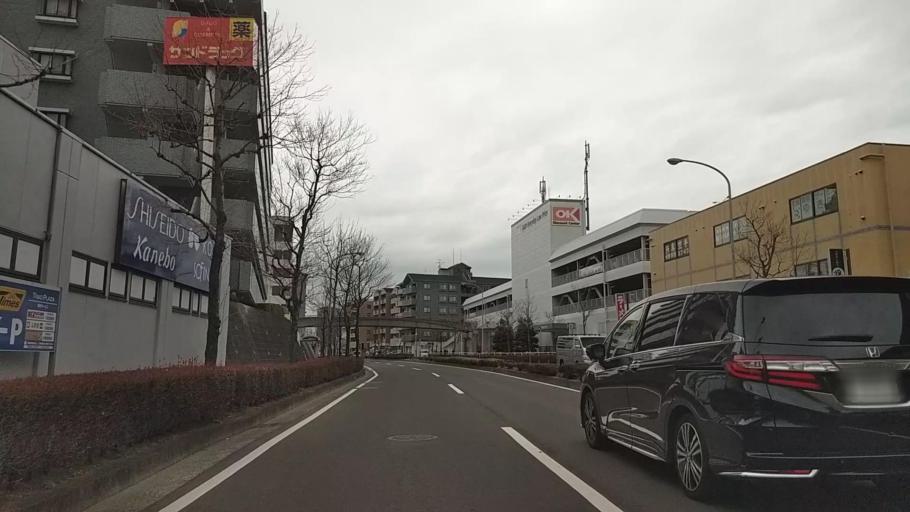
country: JP
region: Tokyo
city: Chofugaoka
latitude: 35.5598
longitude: 139.5967
